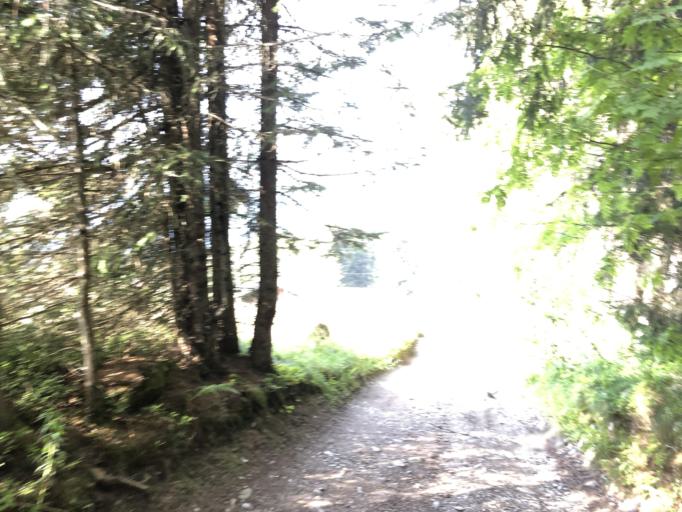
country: FR
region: Rhone-Alpes
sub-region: Departement de la Haute-Savoie
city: Combloux
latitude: 45.8748
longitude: 6.6606
